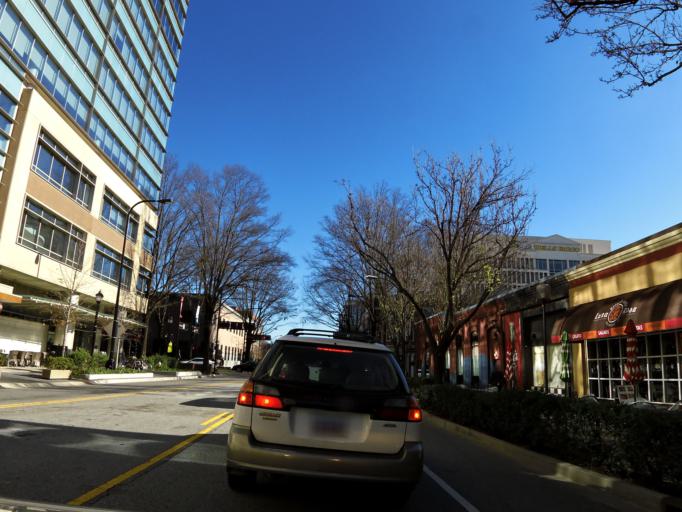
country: US
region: South Carolina
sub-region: Greenville County
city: Greenville
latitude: 34.8509
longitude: -82.3996
